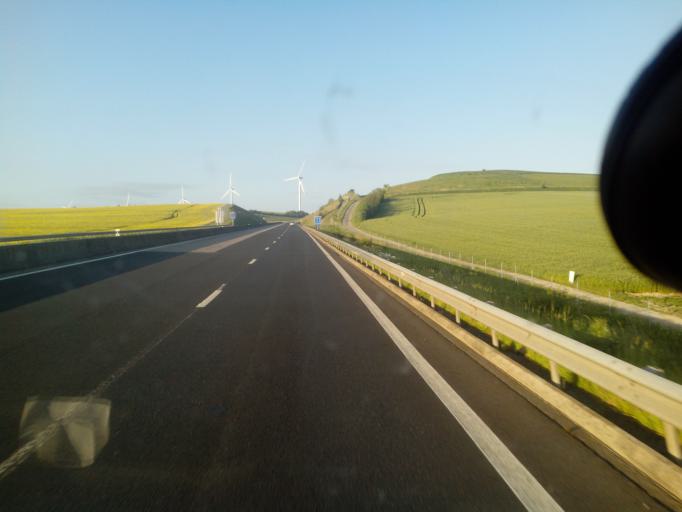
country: FR
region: Haute-Normandie
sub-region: Departement de la Seine-Maritime
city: Neufchatel-en-Bray
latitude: 49.7881
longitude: 1.4911
